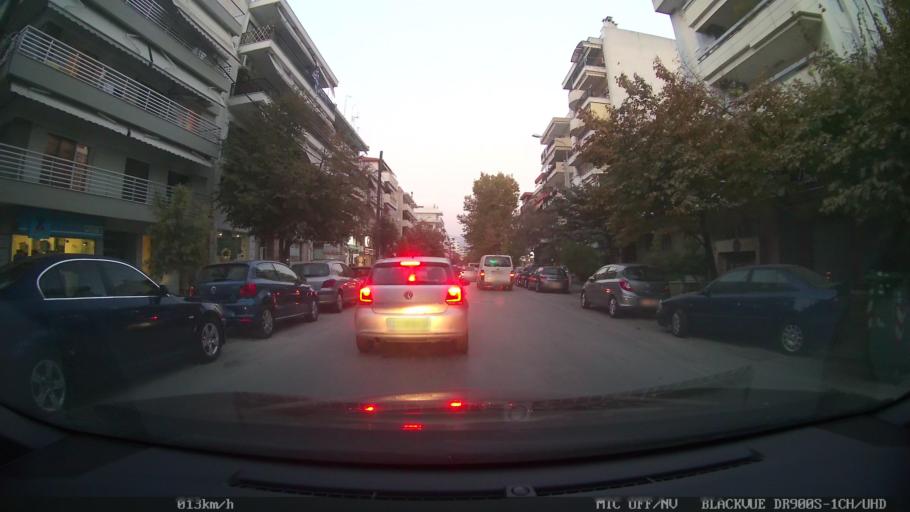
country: GR
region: Central Macedonia
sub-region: Nomos Thessalonikis
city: Kalamaria
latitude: 40.5837
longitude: 22.9573
